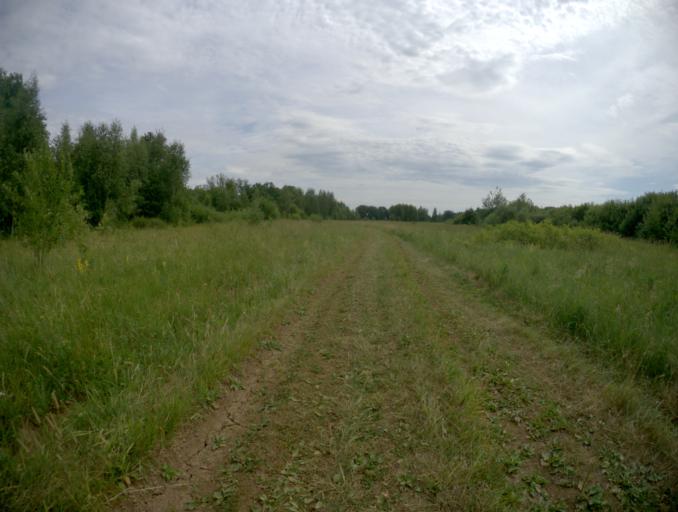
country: RU
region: Vladimir
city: Raduzhnyy
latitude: 56.0316
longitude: 40.2605
